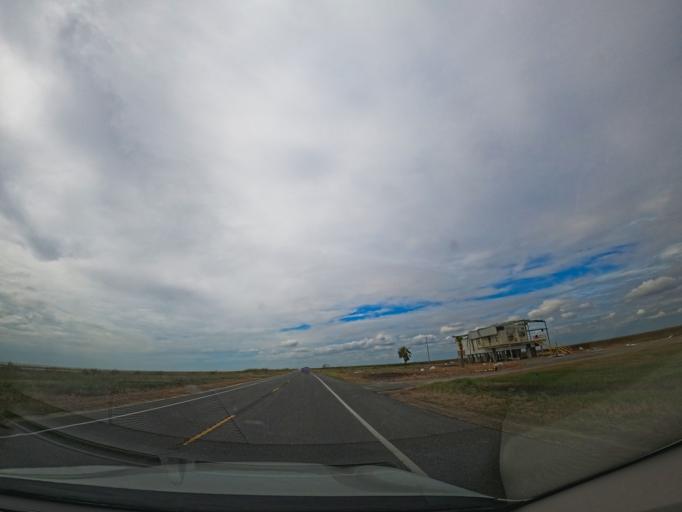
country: US
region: Louisiana
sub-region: Cameron Parish
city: Cameron
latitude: 29.7701
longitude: -93.4775
